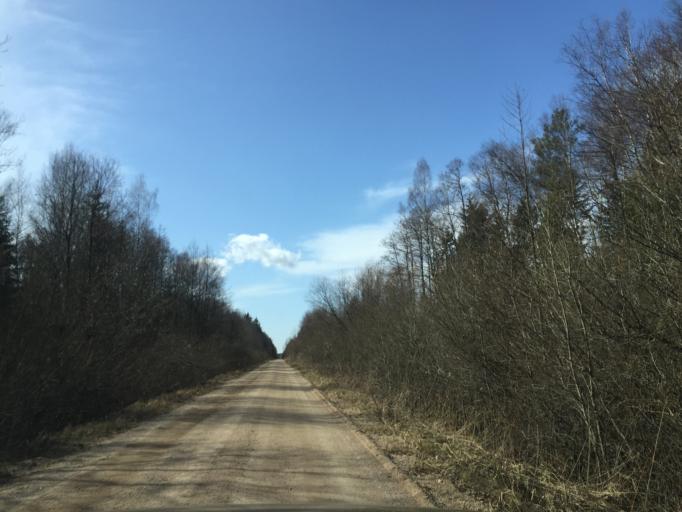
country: LV
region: Ikskile
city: Ikskile
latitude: 56.9243
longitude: 24.4499
